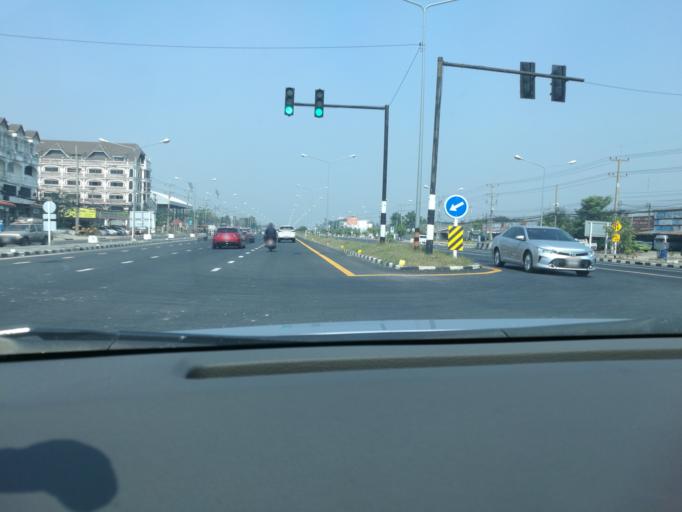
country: TH
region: Sara Buri
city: Saraburi
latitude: 14.5533
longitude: 100.9069
